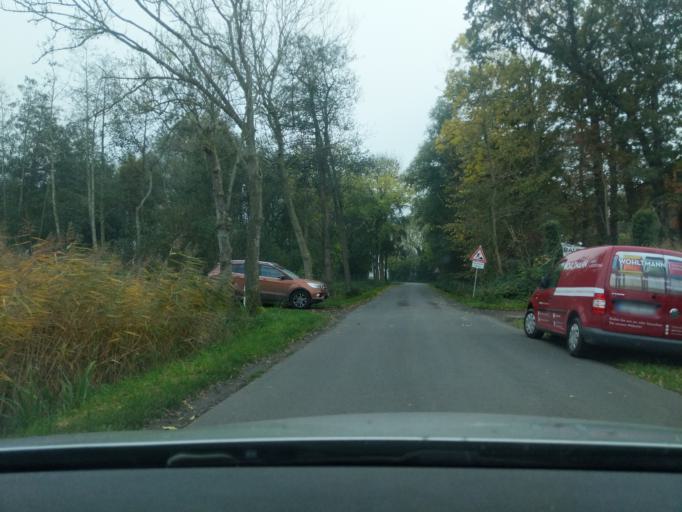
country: DE
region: Lower Saxony
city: Otterndorf
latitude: 53.8225
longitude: 8.8678
